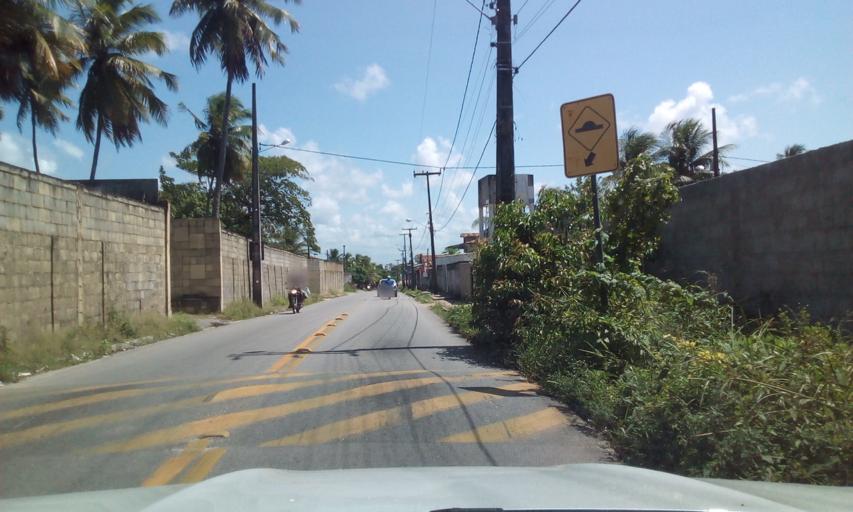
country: BR
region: Paraiba
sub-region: Conde
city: Conde
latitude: -7.2058
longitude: -34.8290
